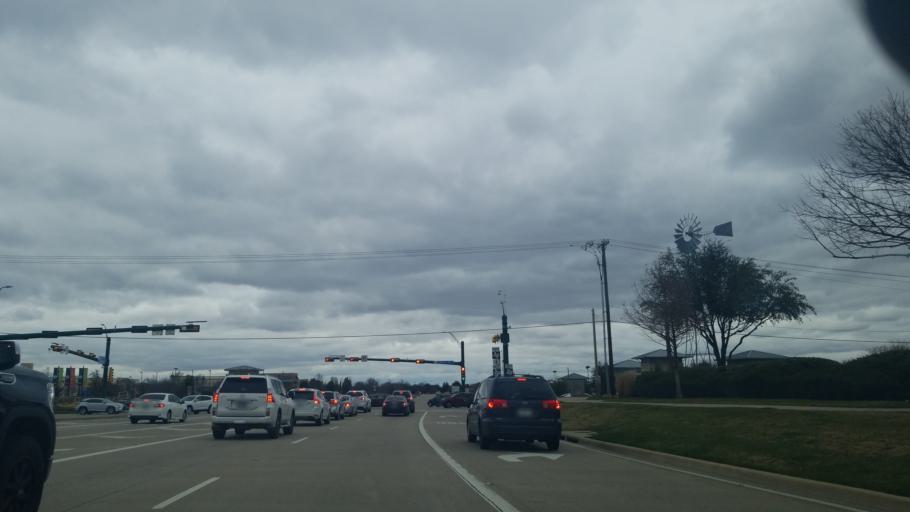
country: US
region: Texas
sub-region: Denton County
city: Double Oak
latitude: 33.0713
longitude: -97.0833
